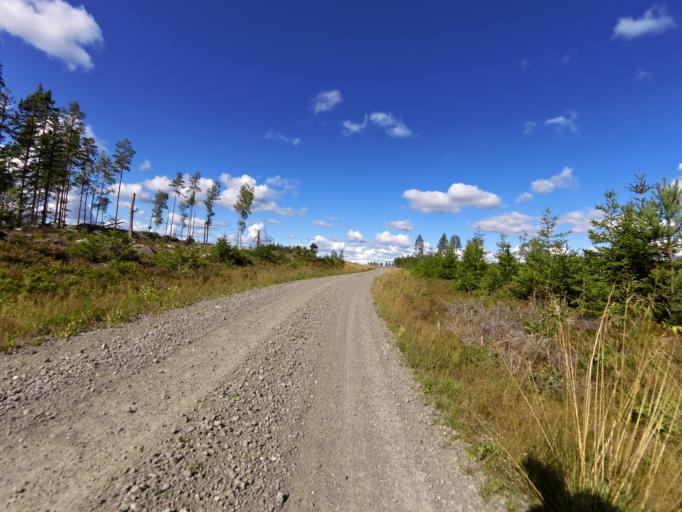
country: SE
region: Gaevleborg
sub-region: Ockelbo Kommun
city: Ockelbo
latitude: 60.8224
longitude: 16.7535
